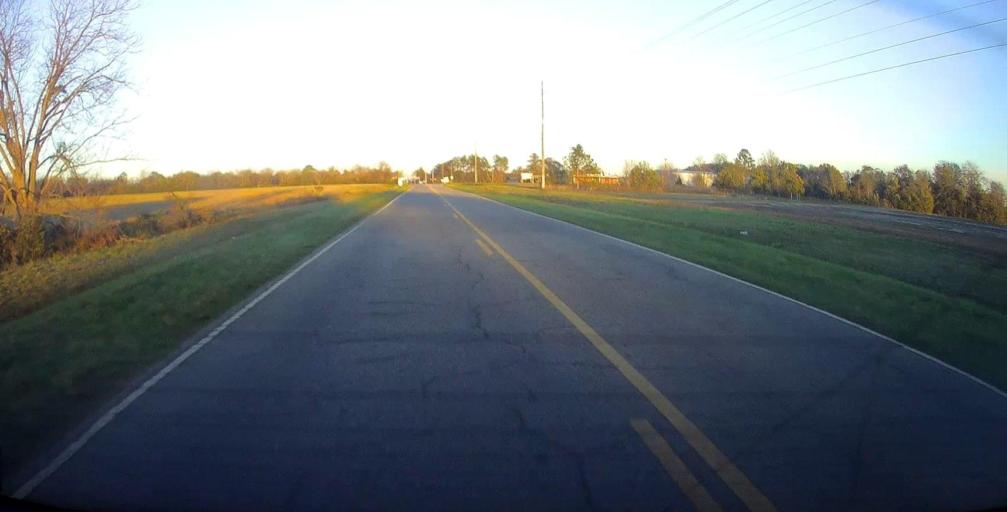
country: US
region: Georgia
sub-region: Crisp County
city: Cordele
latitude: 31.9553
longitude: -83.8005
